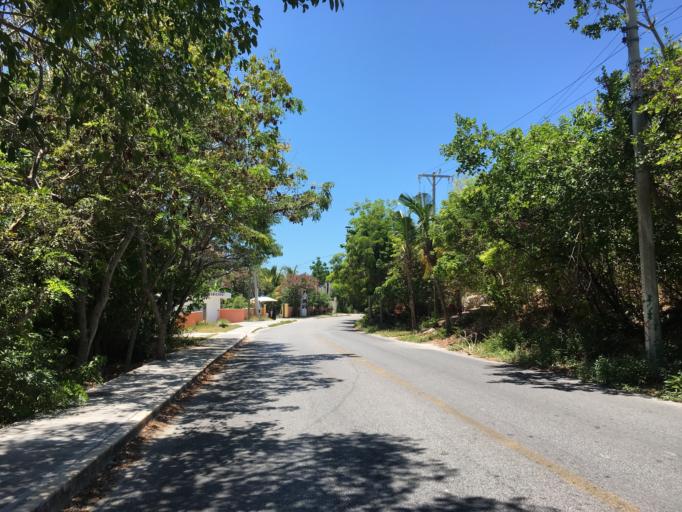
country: MX
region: Quintana Roo
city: Isla Mujeres
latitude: 21.2181
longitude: -86.7274
